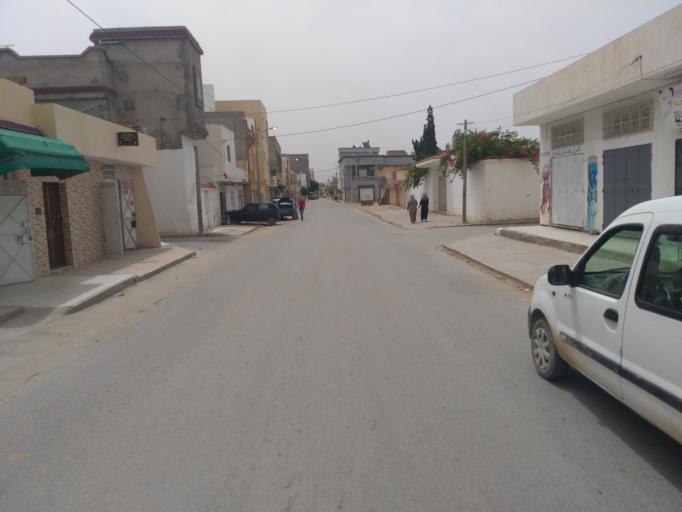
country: TN
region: Al Qayrawan
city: Kairouan
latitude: 35.6690
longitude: 10.0827
